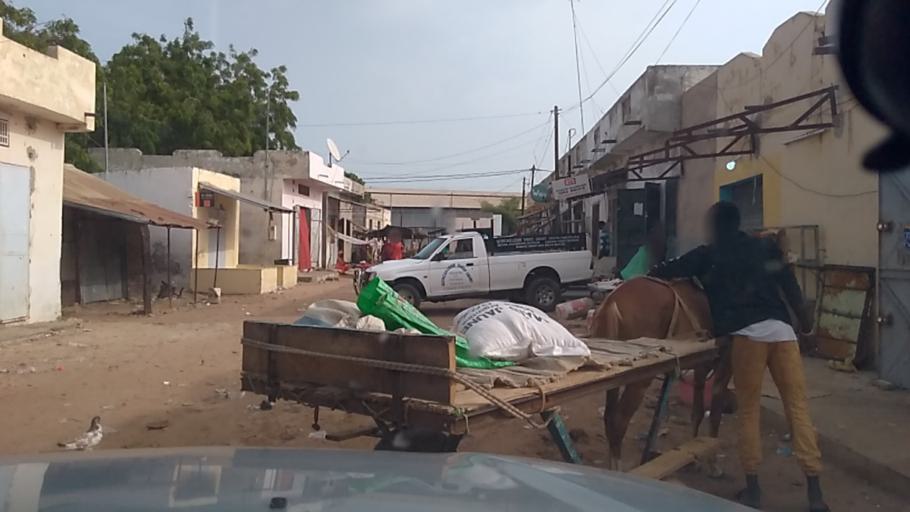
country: SN
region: Diourbel
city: Touba
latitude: 15.1043
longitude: -16.1700
